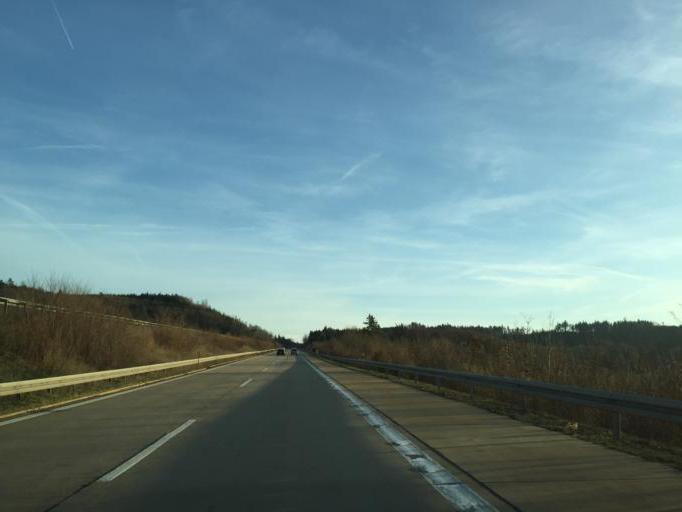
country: DE
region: Bavaria
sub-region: Regierungsbezirk Mittelfranken
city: Schillingsfurst
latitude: 49.2859
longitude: 10.2244
